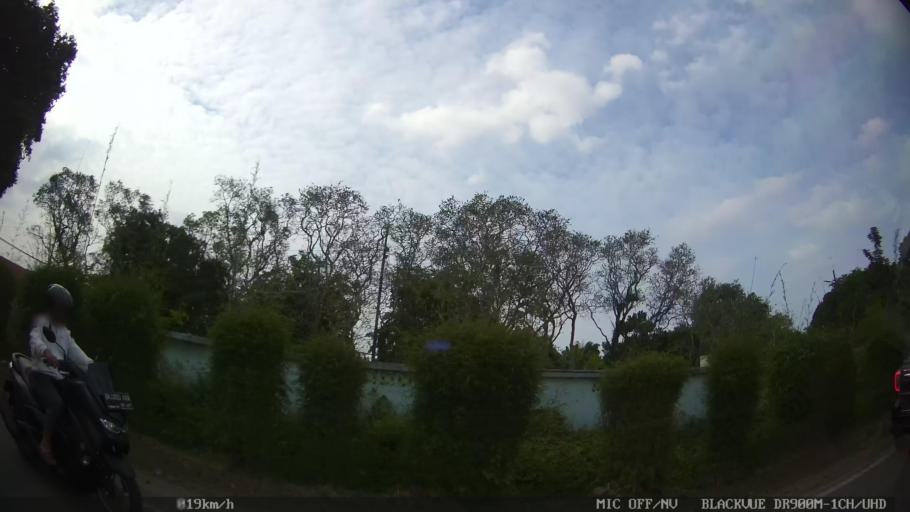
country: ID
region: North Sumatra
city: Medan
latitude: 3.5569
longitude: 98.6818
